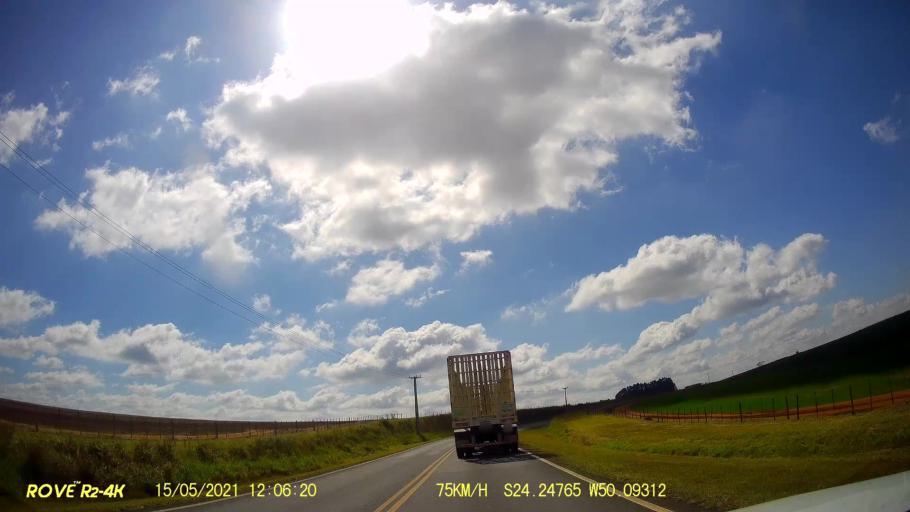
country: BR
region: Parana
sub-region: Pirai Do Sul
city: Pirai do Sul
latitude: -24.2481
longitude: -50.0935
